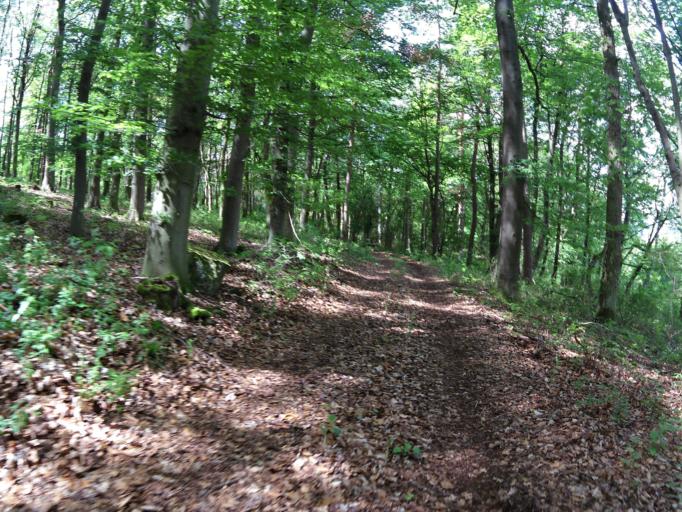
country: DE
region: Bavaria
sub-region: Regierungsbezirk Unterfranken
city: Winterhausen
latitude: 49.7200
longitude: 10.0231
